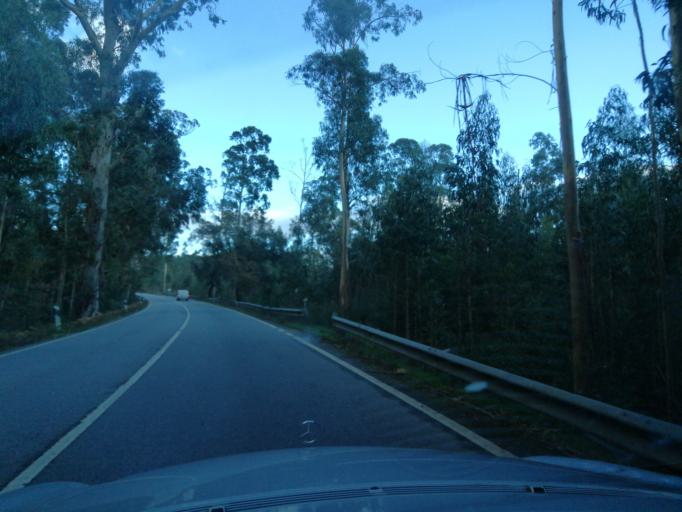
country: PT
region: Braga
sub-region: Esposende
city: Marinhas
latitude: 41.5807
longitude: -8.7305
